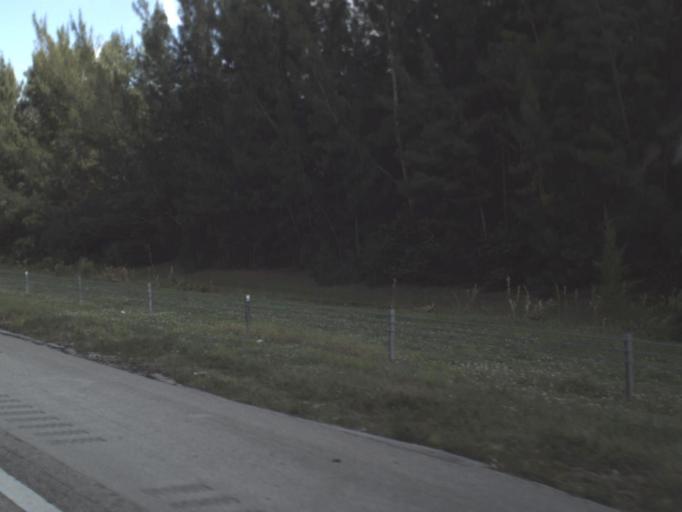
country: US
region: Florida
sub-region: Palm Beach County
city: Schall Circle
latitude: 26.7635
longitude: -80.1336
